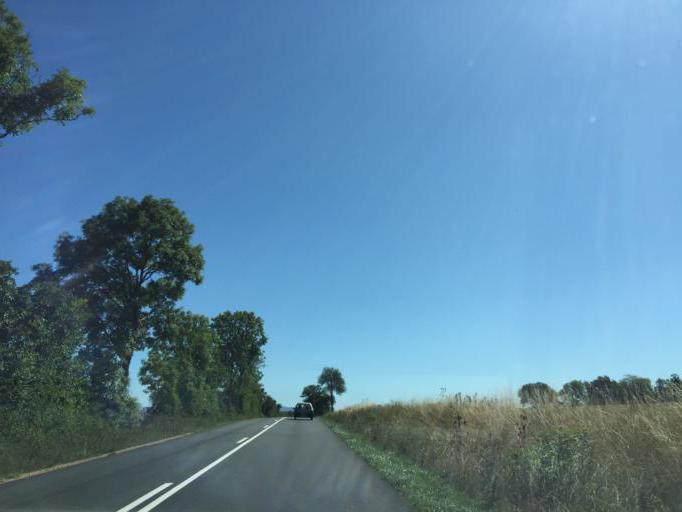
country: FR
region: Midi-Pyrenees
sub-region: Departement de l'Aveyron
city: La Cavalerie
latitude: 44.0154
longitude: 3.0999
